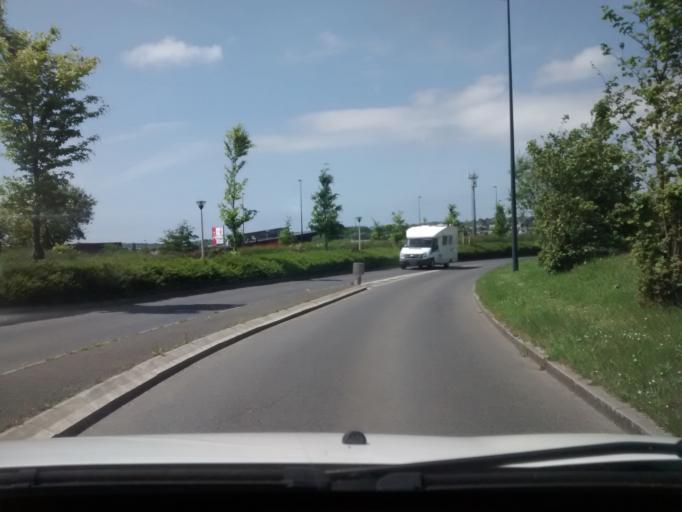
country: FR
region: Brittany
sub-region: Departement des Cotes-d'Armor
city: Lannion
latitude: 48.7343
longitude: -3.4353
